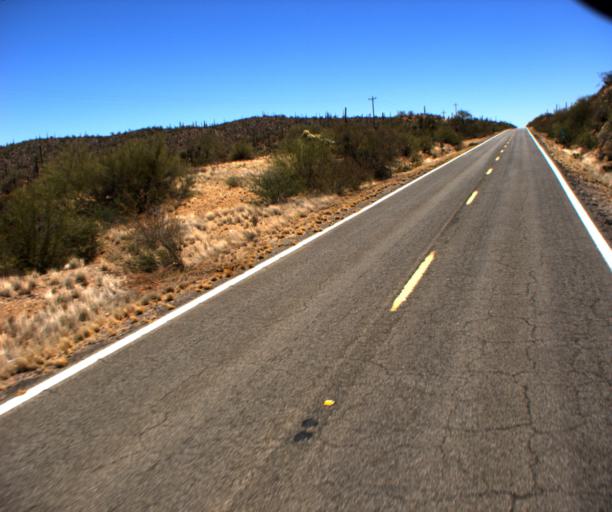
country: US
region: Arizona
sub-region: Pima County
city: Sells
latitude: 32.1747
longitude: -112.1797
